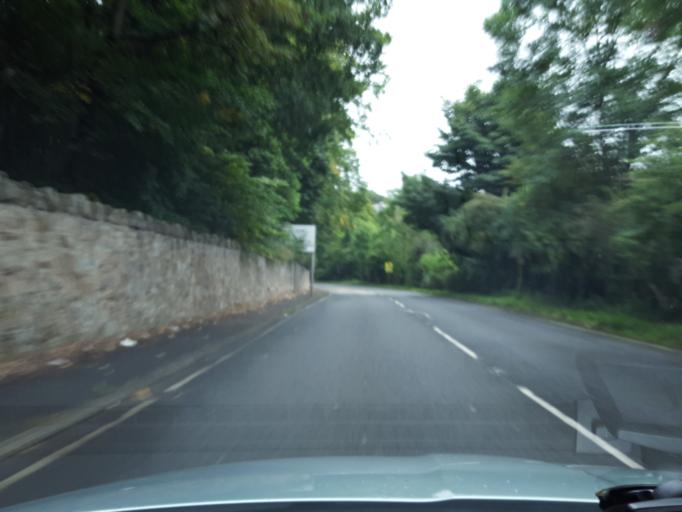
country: GB
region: Scotland
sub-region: Midlothian
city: Bonnyrigg
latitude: 55.8843
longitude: -3.1275
